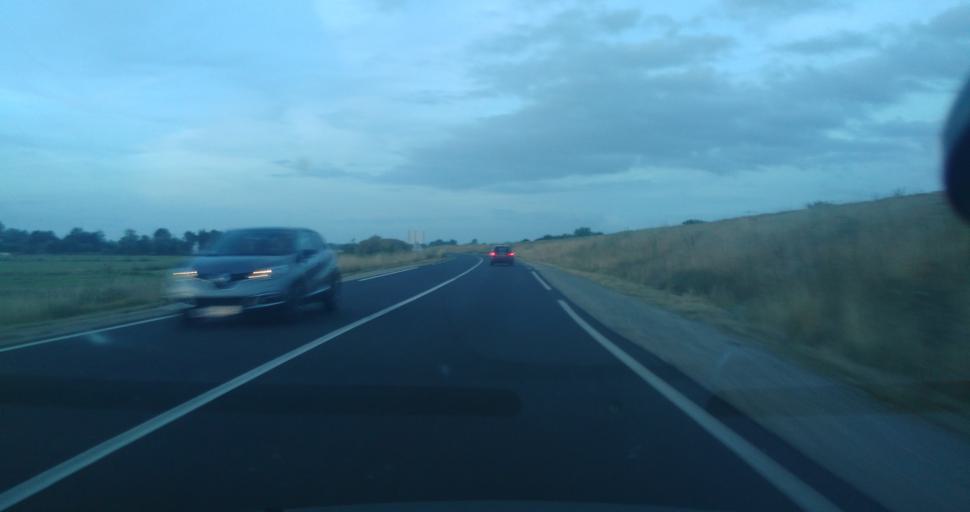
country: FR
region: Pays de la Loire
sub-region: Departement de la Vendee
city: Le Perrier
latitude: 46.8050
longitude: -1.9829
